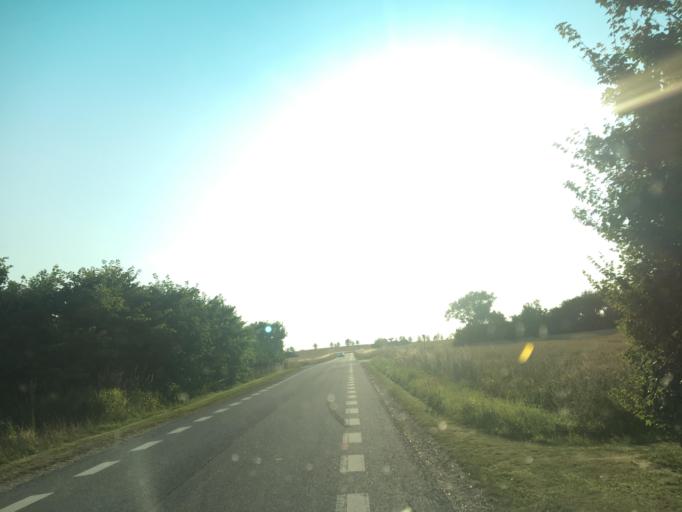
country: DK
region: North Denmark
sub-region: Thisted Kommune
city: Hurup
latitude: 56.8165
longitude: 8.3787
